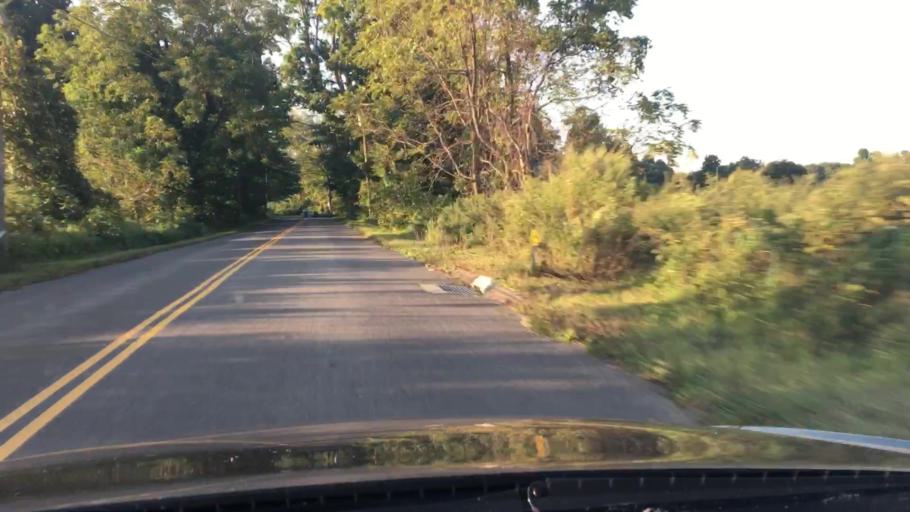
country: US
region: Connecticut
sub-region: Litchfield County
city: New Milford
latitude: 41.5995
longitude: -73.3738
